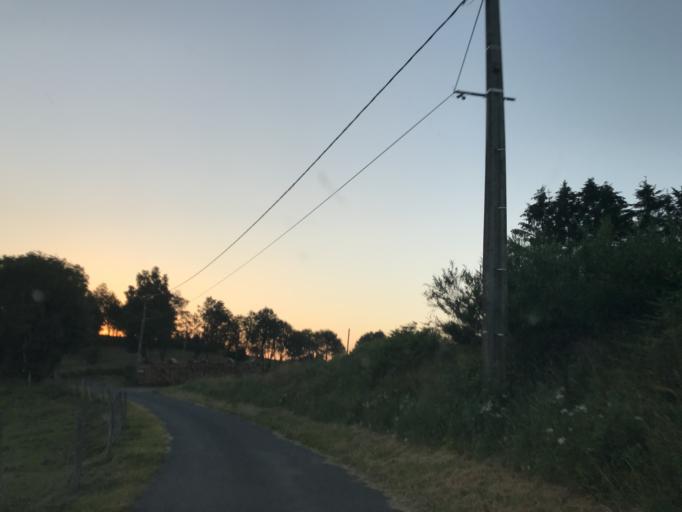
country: FR
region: Rhone-Alpes
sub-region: Departement de la Loire
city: Noiretable
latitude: 45.7719
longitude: 3.7067
